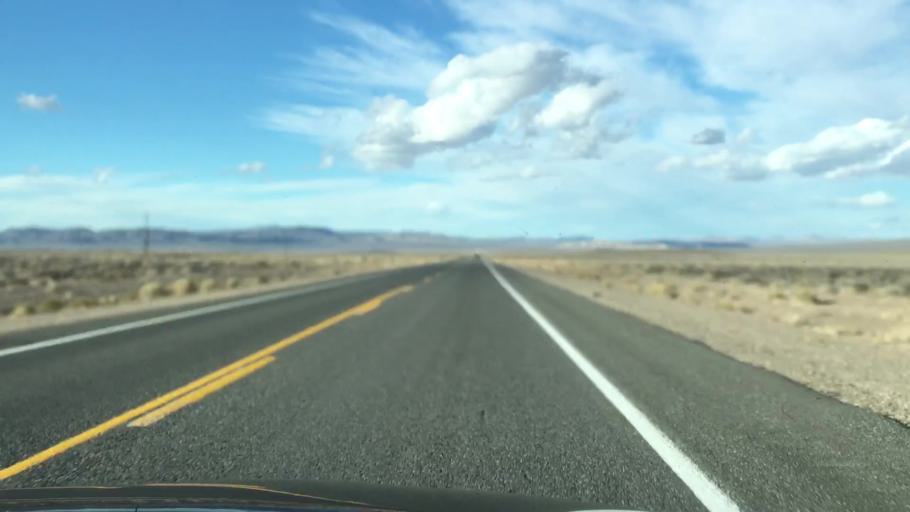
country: US
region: Nevada
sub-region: Esmeralda County
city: Goldfield
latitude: 37.3945
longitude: -117.1464
